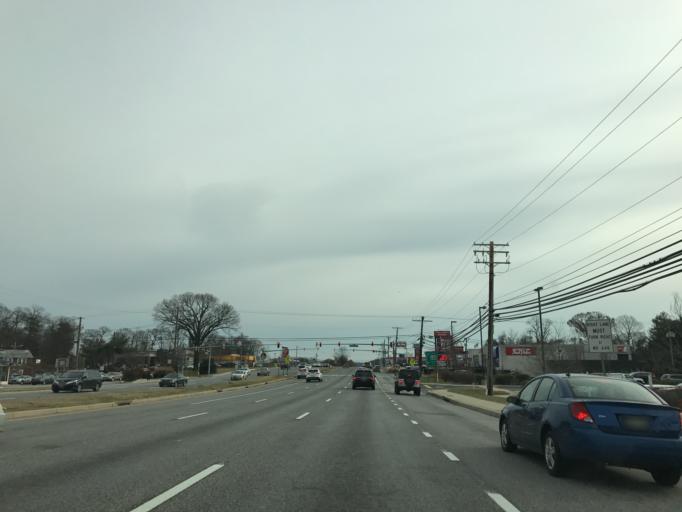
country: US
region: Maryland
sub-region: Anne Arundel County
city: Severna Park
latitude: 39.0817
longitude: -76.5498
